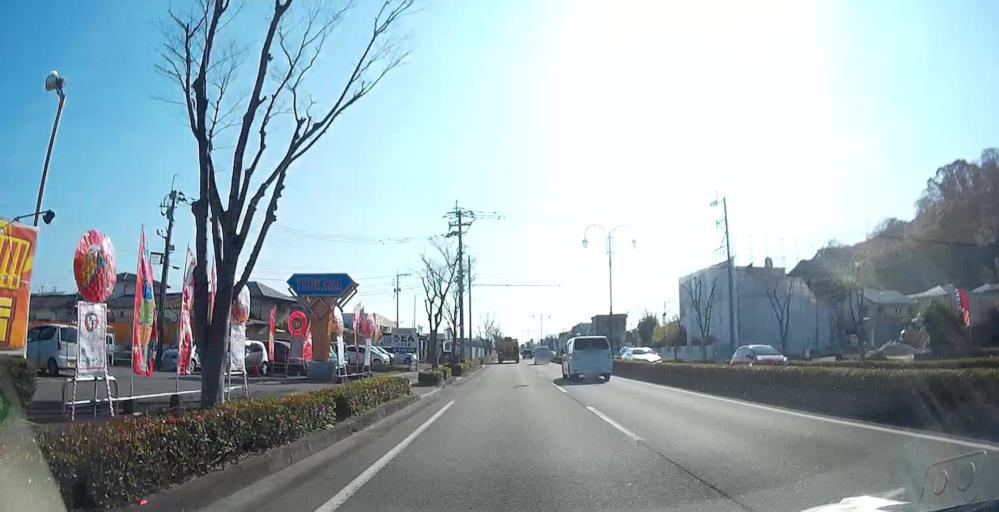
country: JP
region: Kumamoto
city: Kumamoto
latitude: 32.7869
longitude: 130.6734
